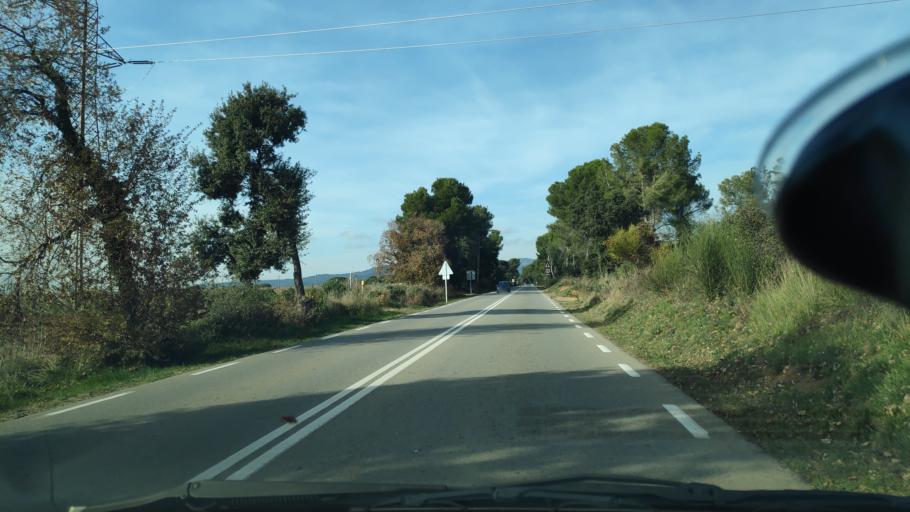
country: ES
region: Catalonia
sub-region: Provincia de Barcelona
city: Matadepera
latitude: 41.5880
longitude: 2.0487
